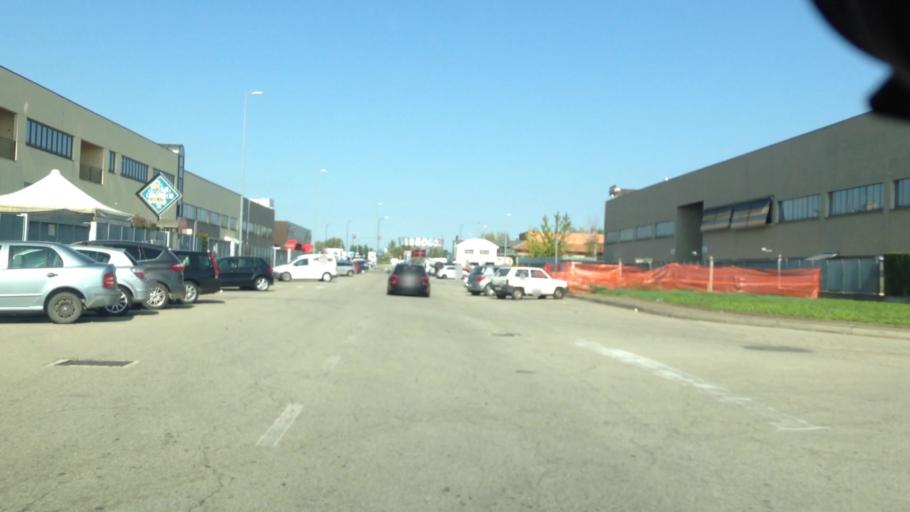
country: IT
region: Piedmont
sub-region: Provincia di Asti
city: Asti
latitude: 44.9037
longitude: 8.2317
